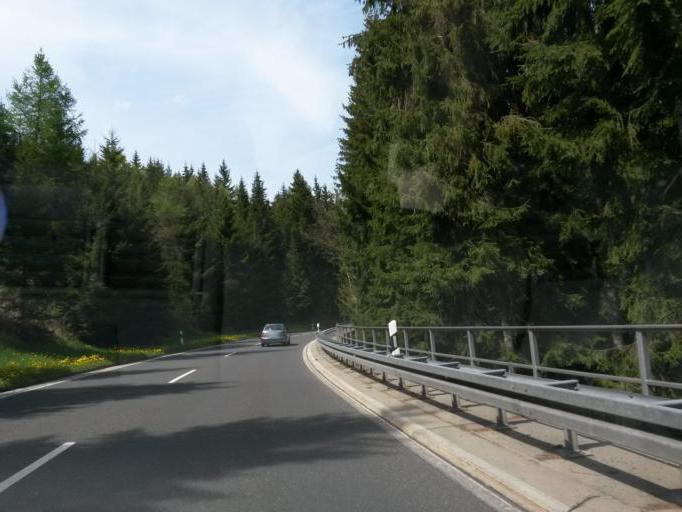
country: DE
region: Saxony
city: Zwota
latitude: 50.3582
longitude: 12.4206
